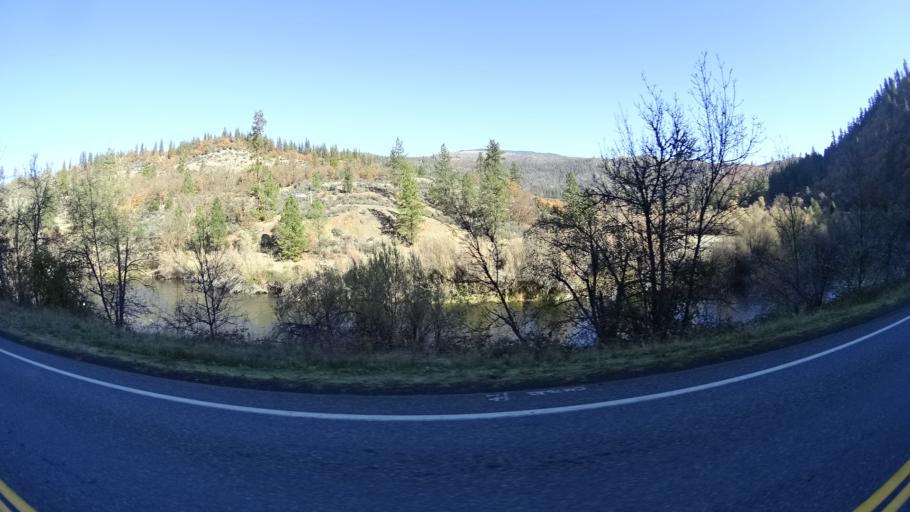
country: US
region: California
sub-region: Siskiyou County
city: Yreka
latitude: 41.8240
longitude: -122.9874
